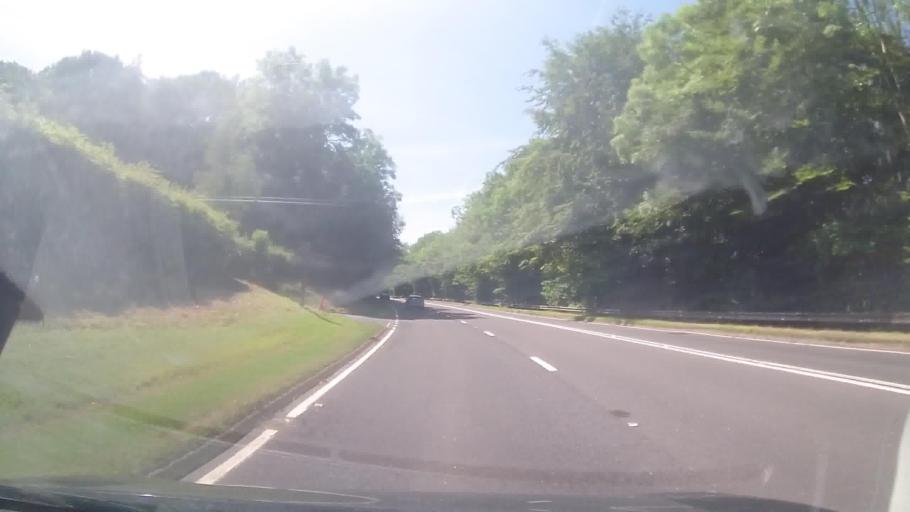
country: GB
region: England
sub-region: Herefordshire
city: Hope under Dinmore
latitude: 52.1709
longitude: -2.7190
